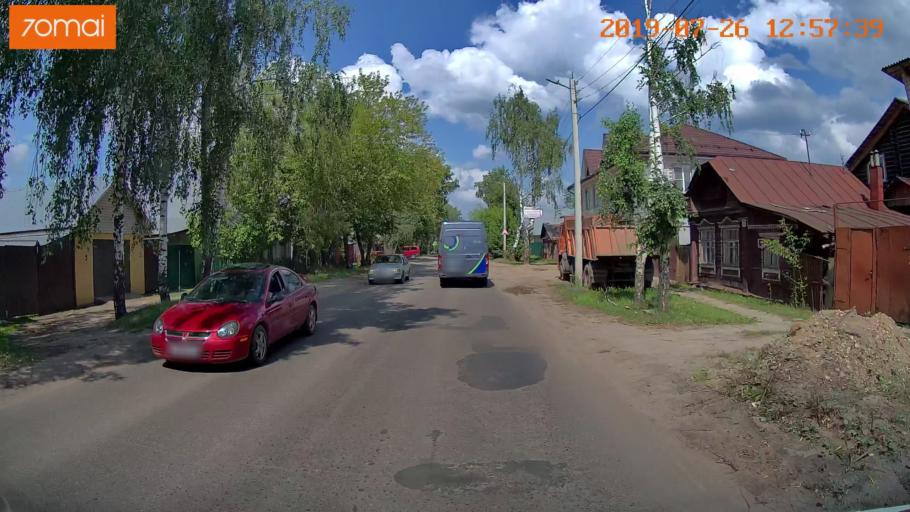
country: RU
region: Ivanovo
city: Bogorodskoye
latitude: 57.0205
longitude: 41.0208
